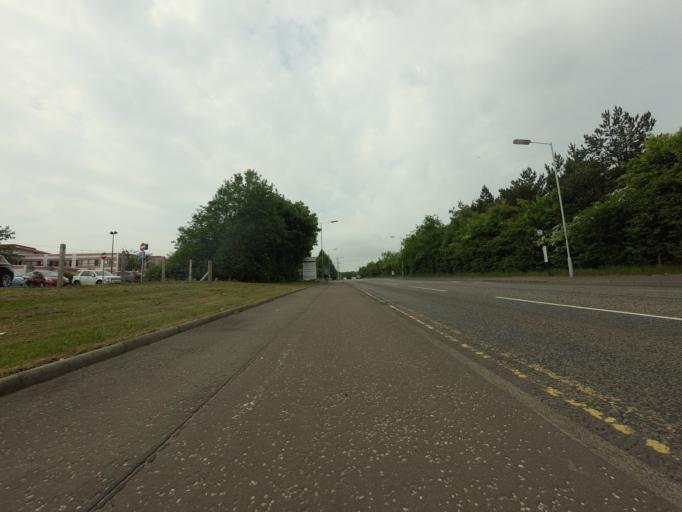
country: GB
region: Scotland
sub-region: Fife
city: Townhill
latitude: 56.0820
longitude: -3.4251
